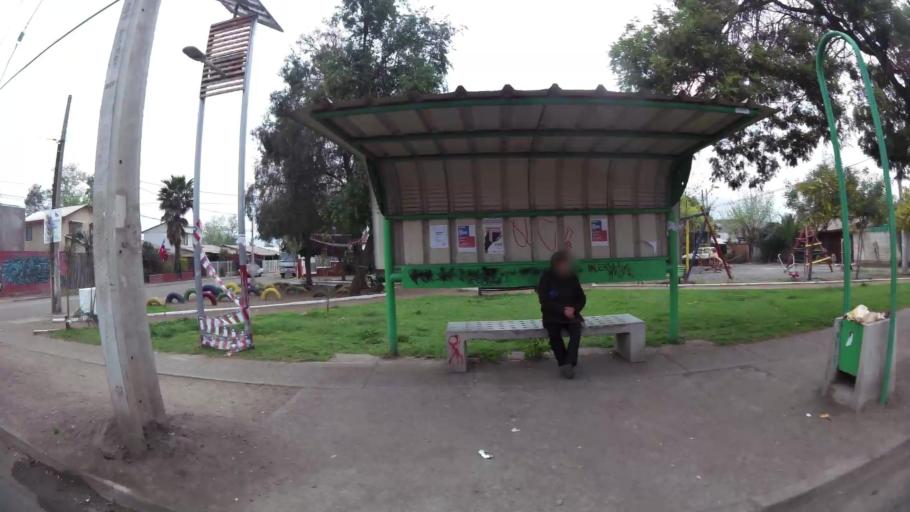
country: CL
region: Santiago Metropolitan
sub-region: Provincia de Chacabuco
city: Chicureo Abajo
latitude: -33.1934
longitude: -70.6752
